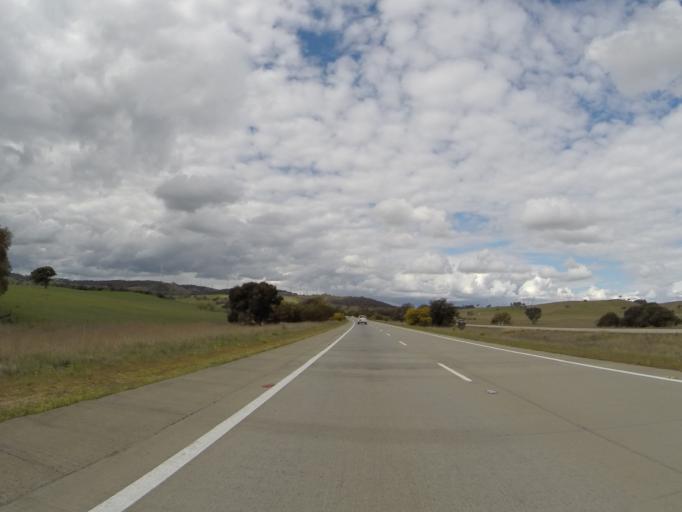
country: AU
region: New South Wales
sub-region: Yass Valley
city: Gundaroo
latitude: -34.8215
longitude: 149.3719
